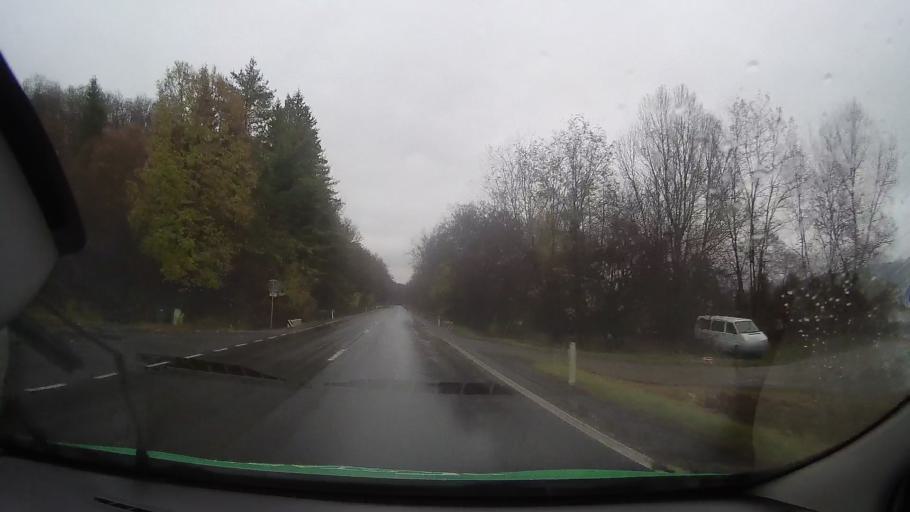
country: RO
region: Mures
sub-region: Comuna Brancovenesti
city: Brancovenesti
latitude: 46.8714
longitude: 24.7722
